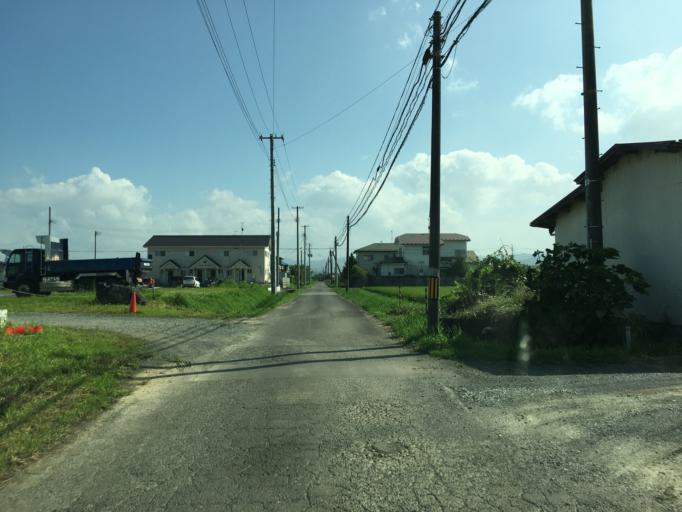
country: JP
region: Miyagi
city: Kakuda
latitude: 37.9535
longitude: 140.7802
